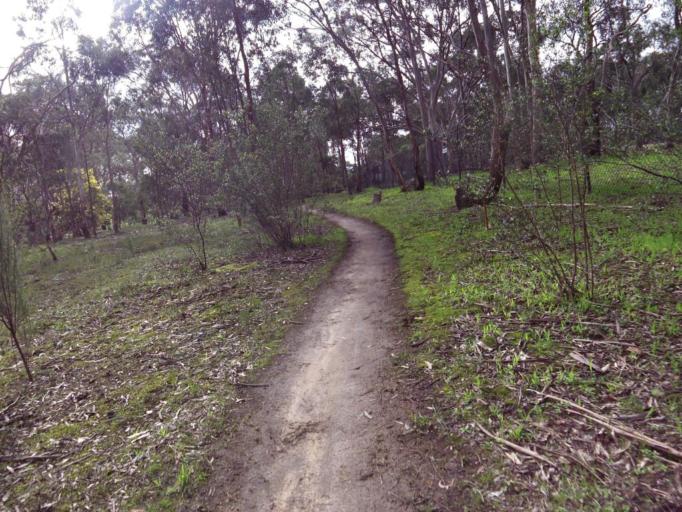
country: AU
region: Victoria
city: Plenty
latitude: -37.6705
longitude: 145.1022
